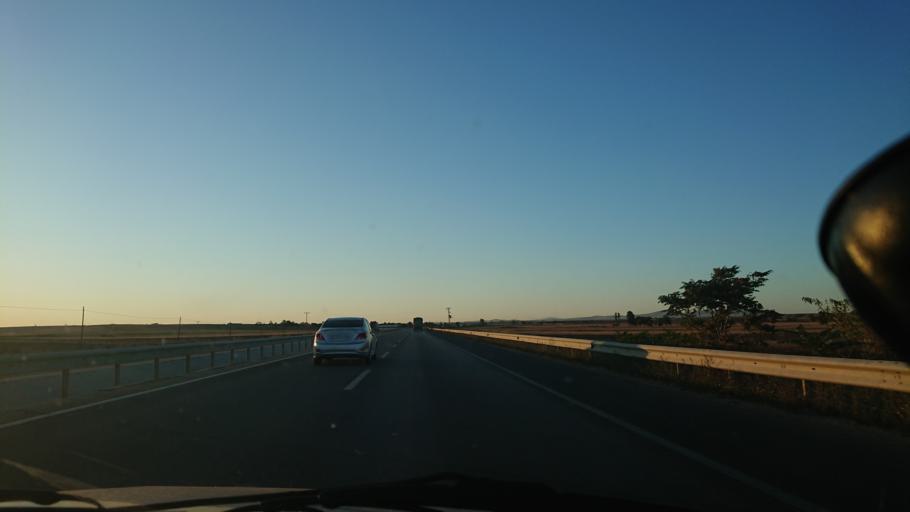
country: TR
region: Eskisehir
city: Mahmudiye
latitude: 39.5270
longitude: 30.9530
